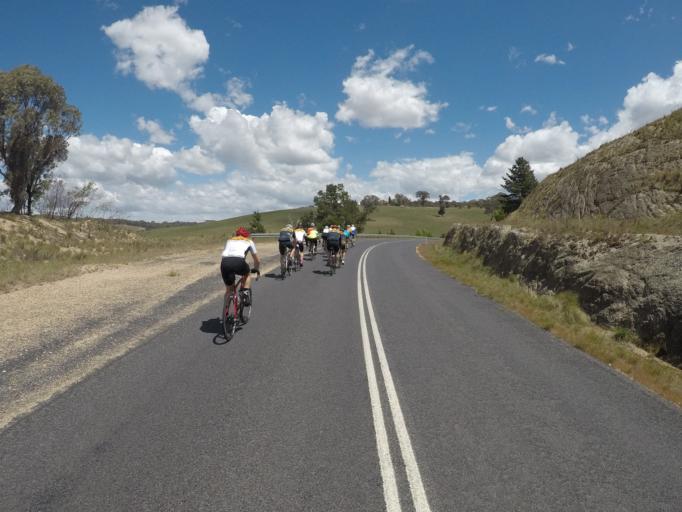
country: AU
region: New South Wales
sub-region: Blayney
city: Blayney
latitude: -33.5793
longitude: 149.4035
